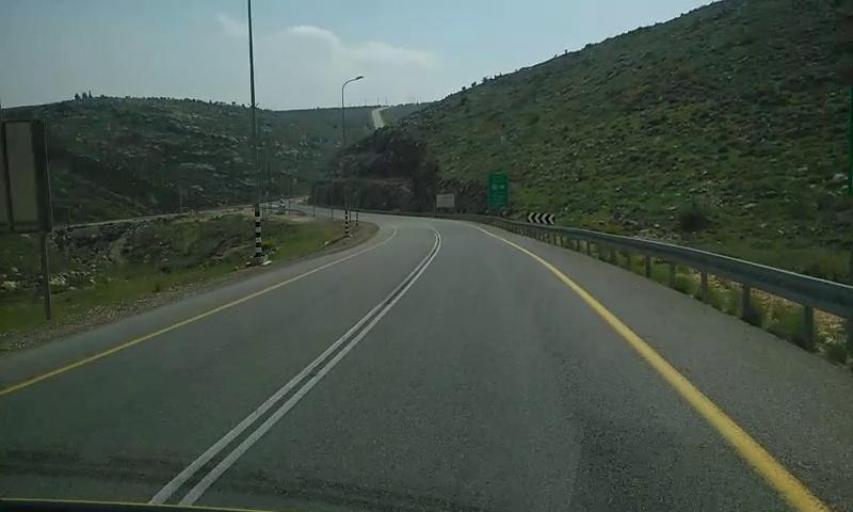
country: PS
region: West Bank
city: Majdal Bani Fadil
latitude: 32.0749
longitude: 35.3525
